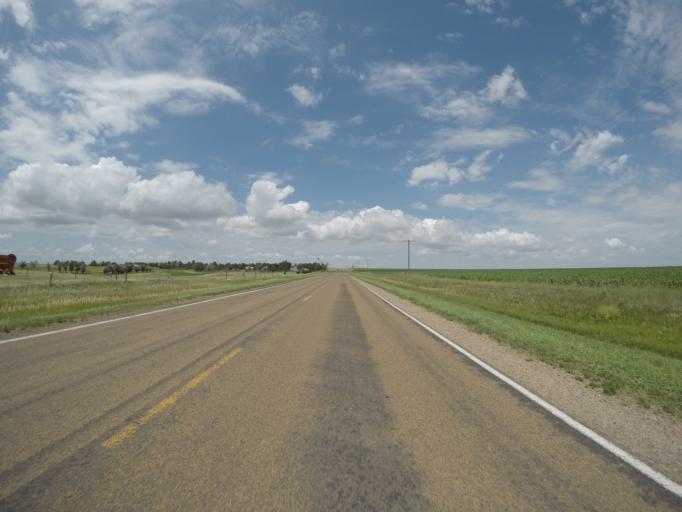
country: US
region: Kansas
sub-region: Rawlins County
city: Atwood
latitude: 39.8578
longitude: -101.0468
